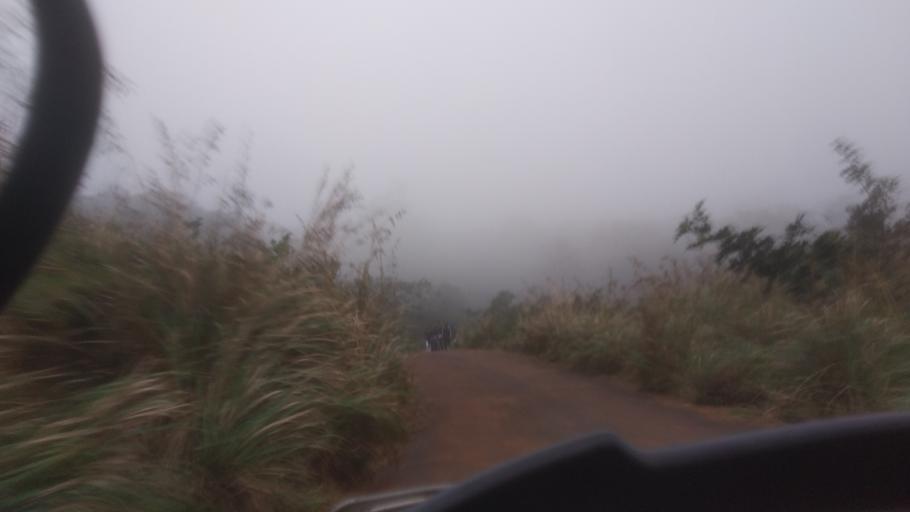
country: IN
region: Tamil Nadu
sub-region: Theni
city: Kombai
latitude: 9.8906
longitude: 77.2216
